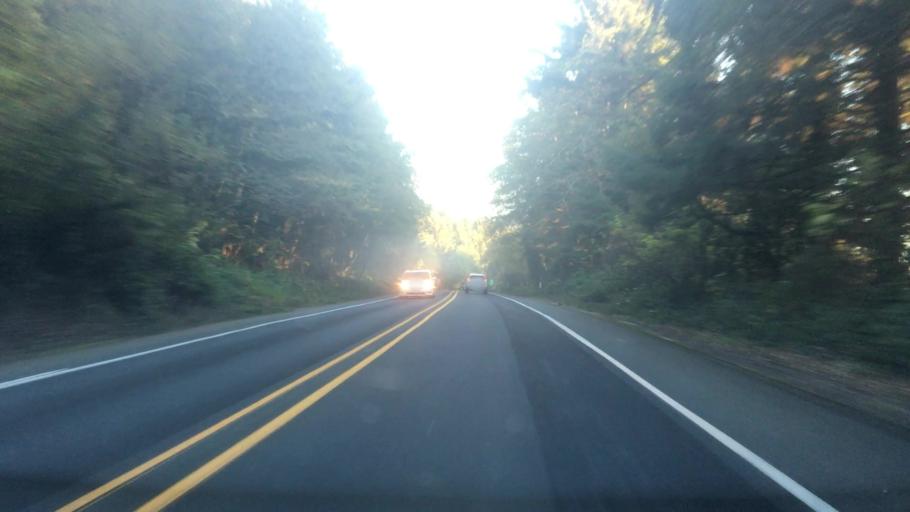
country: US
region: Oregon
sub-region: Clatsop County
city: Cannon Beach
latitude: 45.8821
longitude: -123.9589
